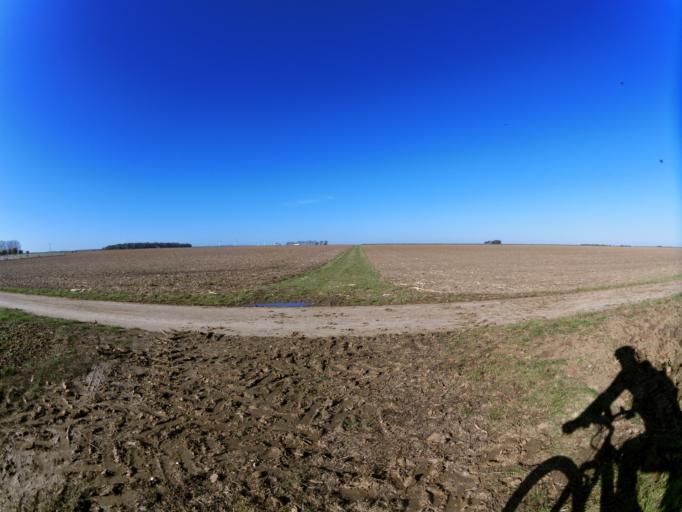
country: DE
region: Bavaria
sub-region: Regierungsbezirk Unterfranken
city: Giebelstadt
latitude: 49.6625
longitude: 9.9331
